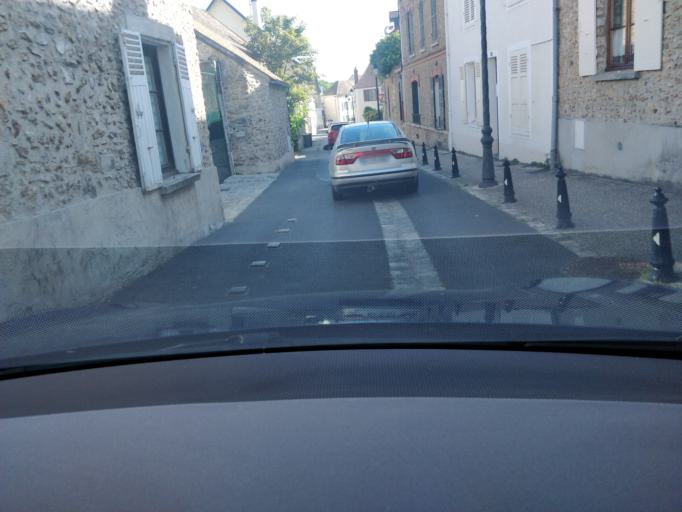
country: FR
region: Ile-de-France
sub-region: Departement de l'Essonne
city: Briis-sous-Forges
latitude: 48.6250
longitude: 2.1231
